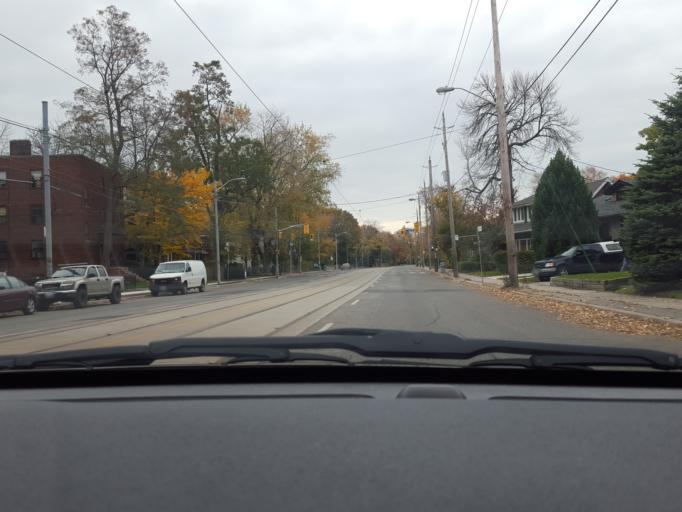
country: CA
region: Ontario
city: Etobicoke
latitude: 43.6094
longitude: -79.4904
